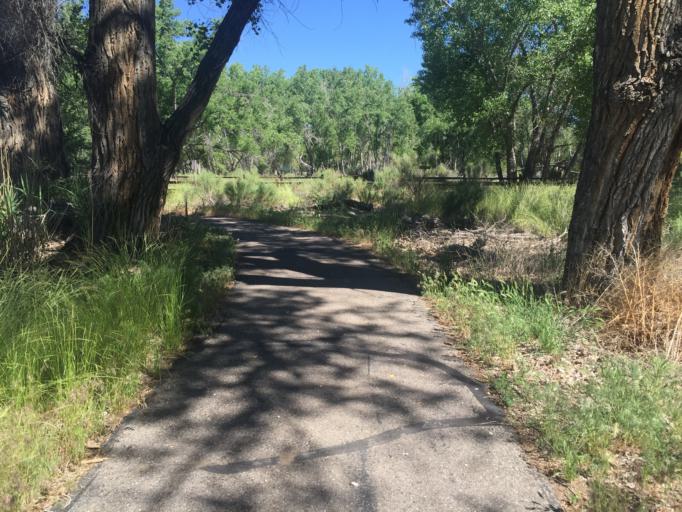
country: US
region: Colorado
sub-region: Mesa County
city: Redlands
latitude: 39.0771
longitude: -108.6071
